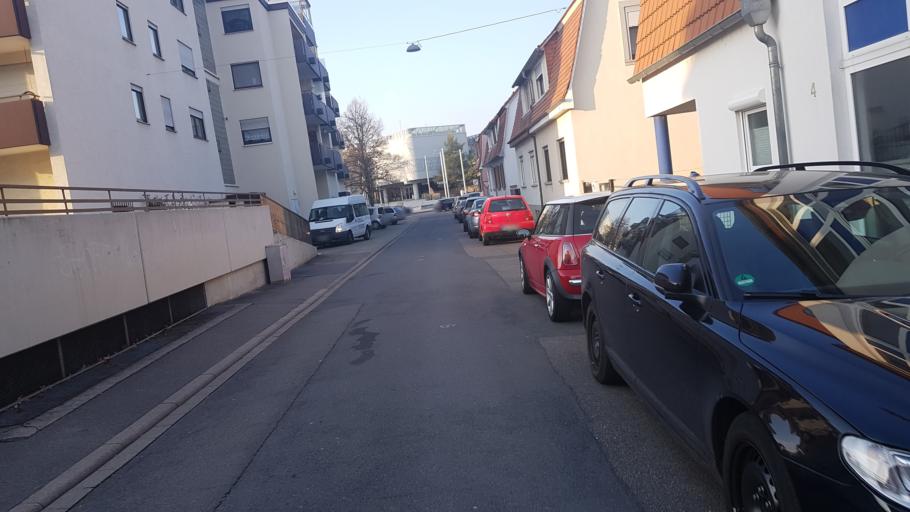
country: DE
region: Baden-Wuerttemberg
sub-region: Karlsruhe Region
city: Walldorf
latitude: 49.3035
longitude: 8.6468
